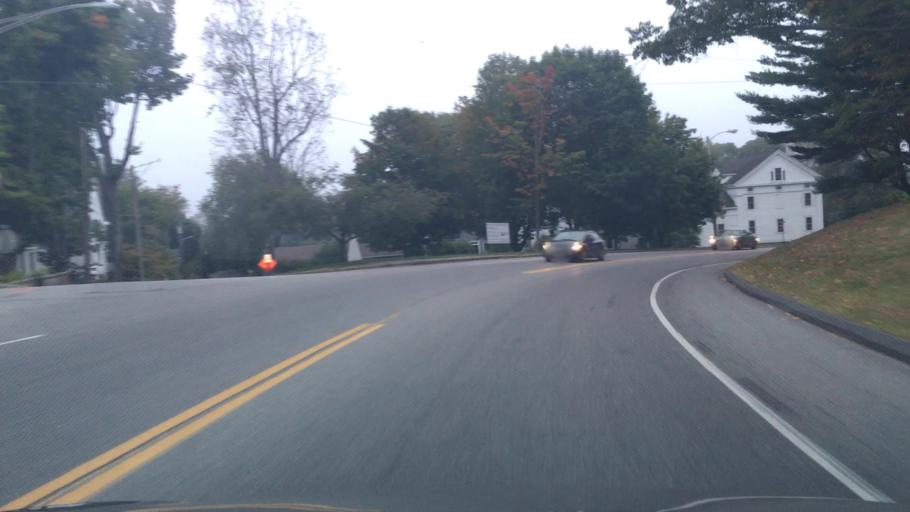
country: US
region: Maine
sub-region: Lincoln County
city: Wiscasset
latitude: 44.0047
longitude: -69.6677
